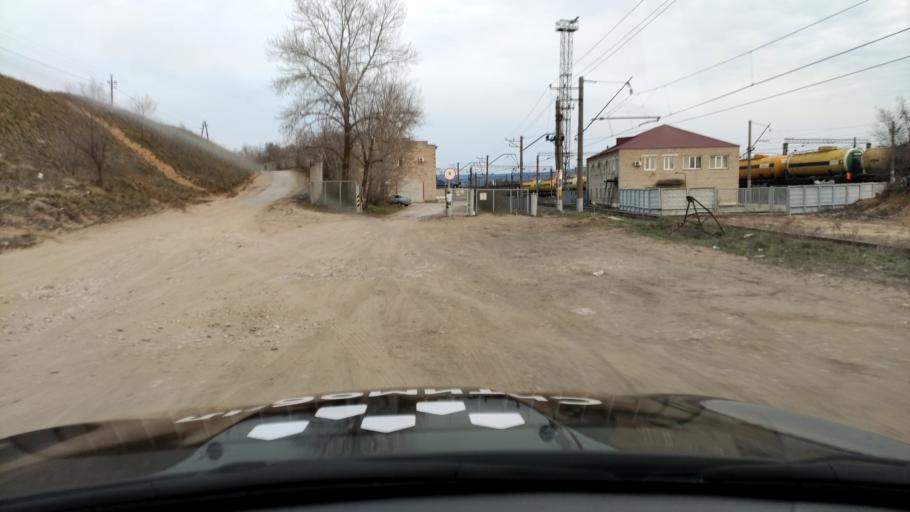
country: RU
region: Samara
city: Zhigulevsk
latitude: 53.4765
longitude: 49.5333
